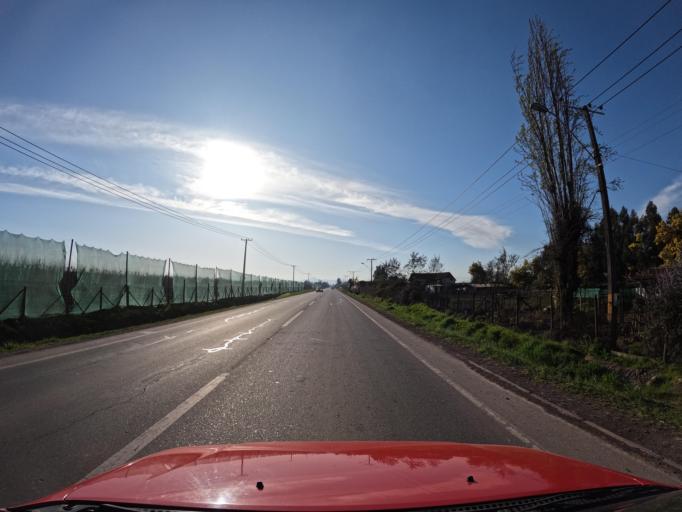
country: CL
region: Maule
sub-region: Provincia de Curico
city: Teno
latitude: -34.8953
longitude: -71.0628
